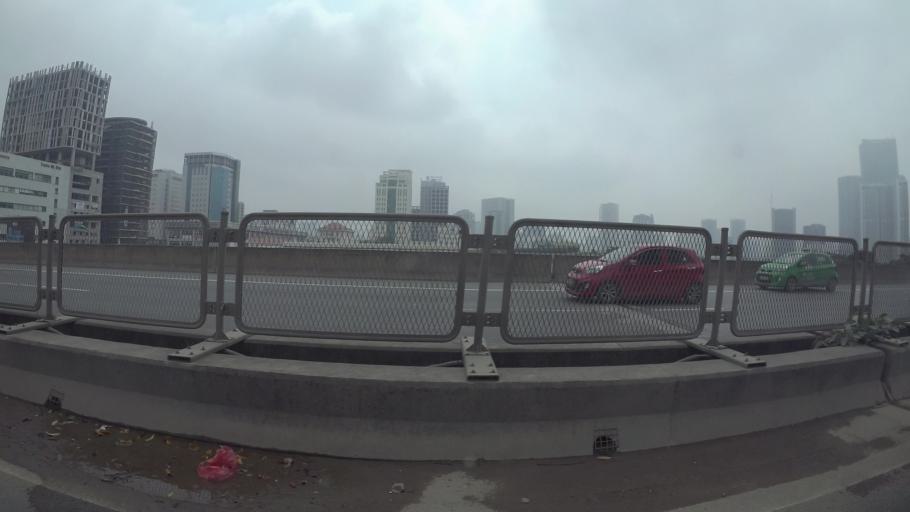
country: VN
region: Ha Noi
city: Cau Dien
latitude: 21.0276
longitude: 105.7791
